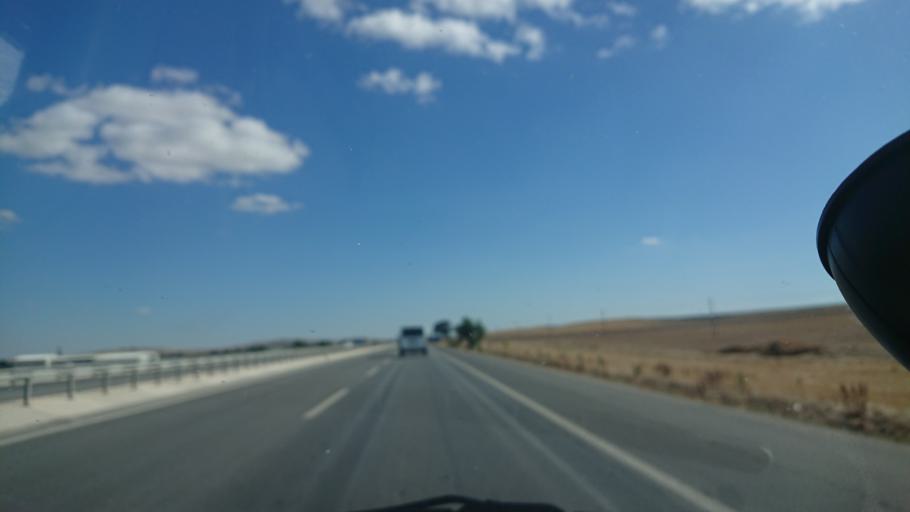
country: TR
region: Eskisehir
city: Mahmudiye
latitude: 39.5287
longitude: 30.9510
